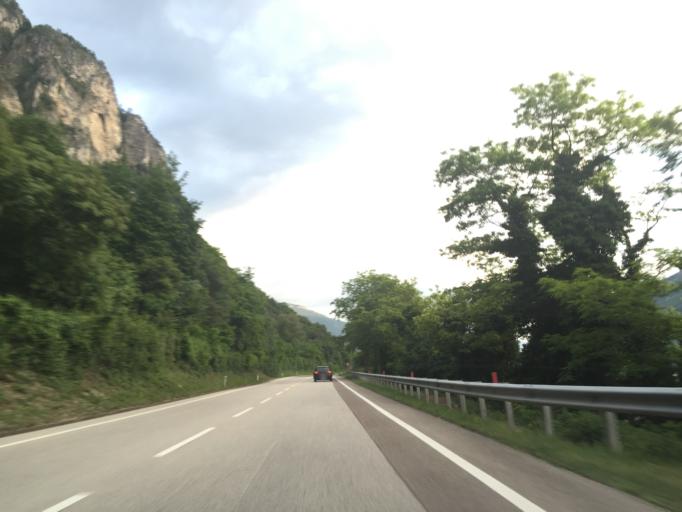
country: IT
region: Trentino-Alto Adige
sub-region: Provincia di Trento
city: Besenello
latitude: 45.9646
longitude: 11.1119
